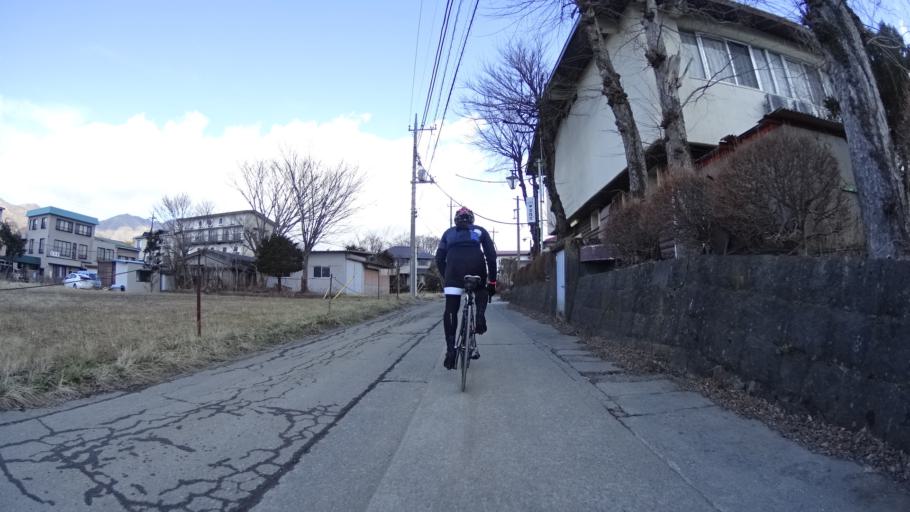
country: JP
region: Shizuoka
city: Gotemba
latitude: 35.4248
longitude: 138.9017
